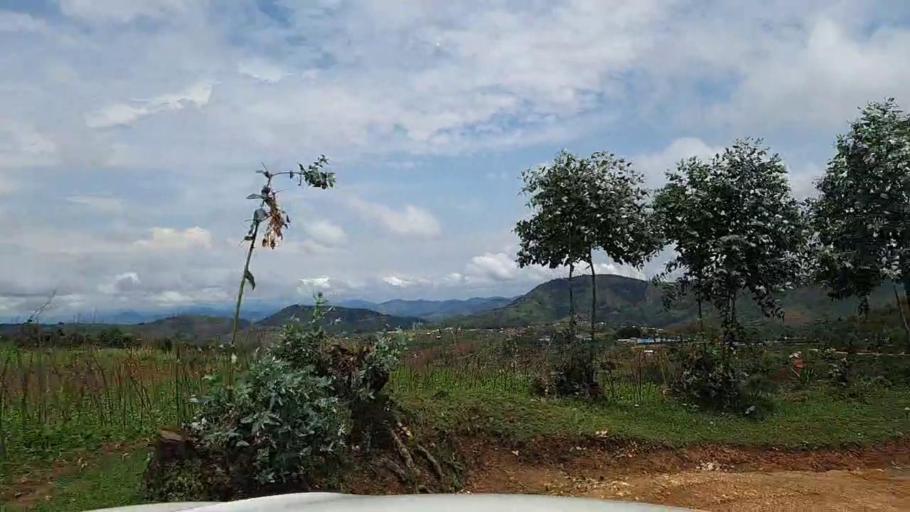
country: RW
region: Southern Province
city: Gikongoro
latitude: -2.3381
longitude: 29.5129
